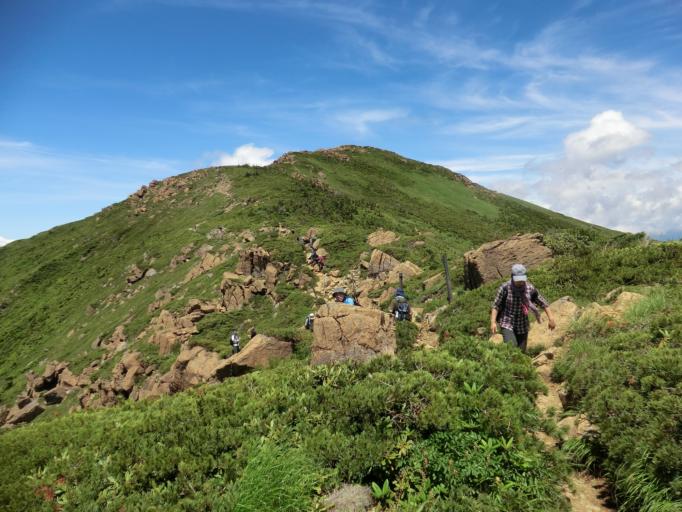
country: JP
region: Gunma
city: Numata
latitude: 36.8974
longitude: 139.1716
